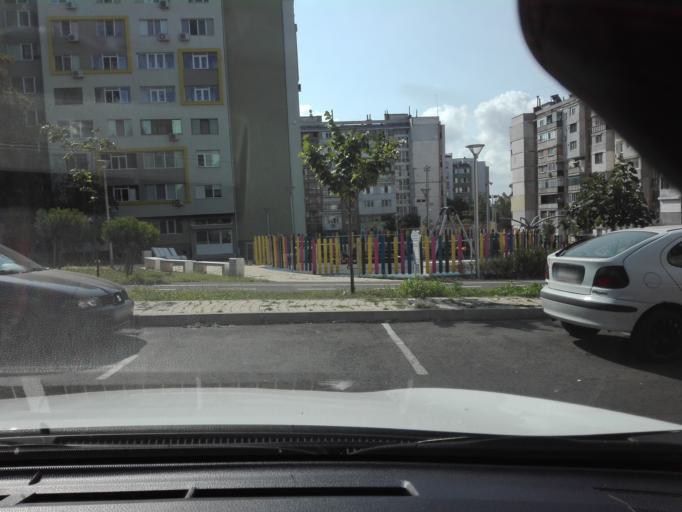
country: BG
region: Burgas
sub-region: Obshtina Burgas
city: Burgas
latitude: 42.4547
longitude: 27.4207
